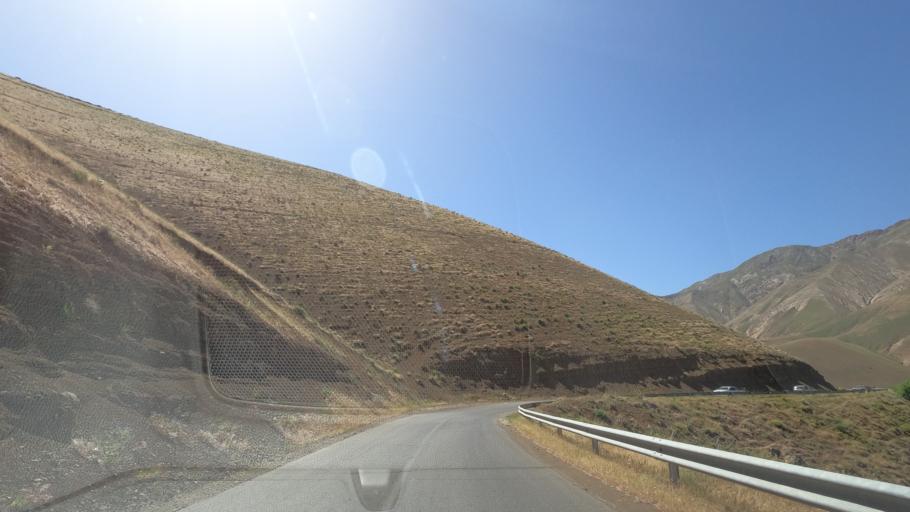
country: IR
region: Alborz
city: Karaj
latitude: 35.9283
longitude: 51.0868
